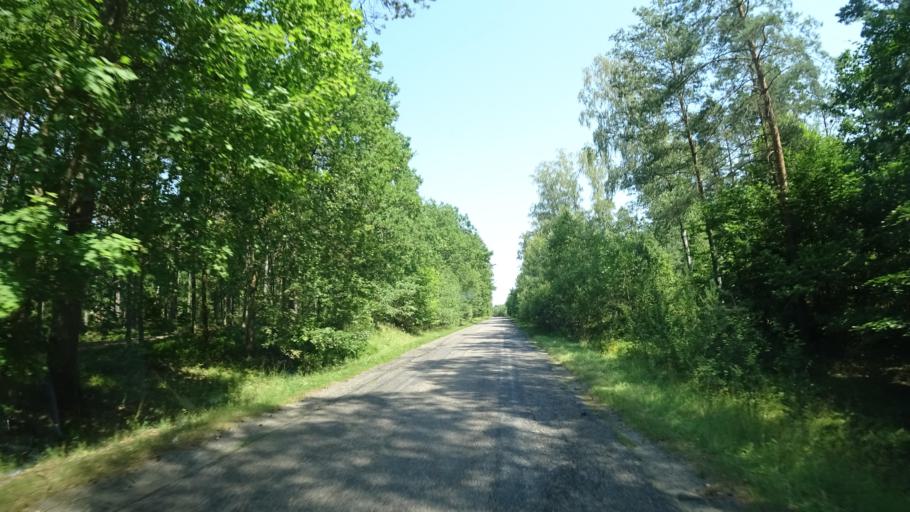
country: PL
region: Pomeranian Voivodeship
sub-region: Powiat chojnicki
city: Brusy
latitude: 53.8728
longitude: 17.6250
